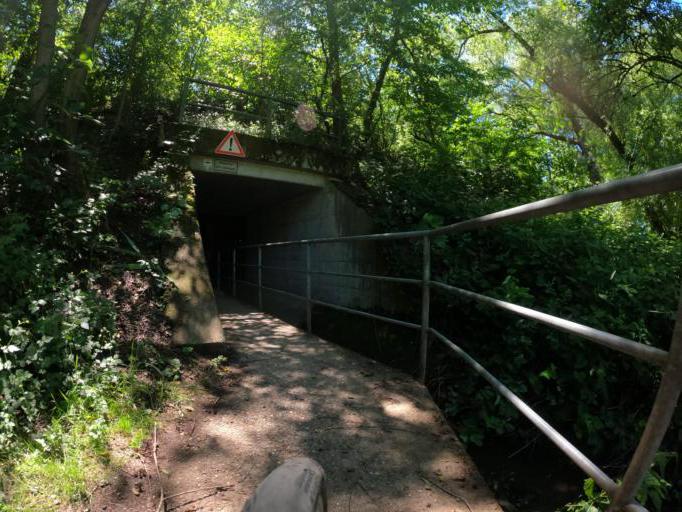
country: DE
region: Baden-Wuerttemberg
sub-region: Regierungsbezirk Stuttgart
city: Vaihingen an der Enz
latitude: 48.9584
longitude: 8.9679
